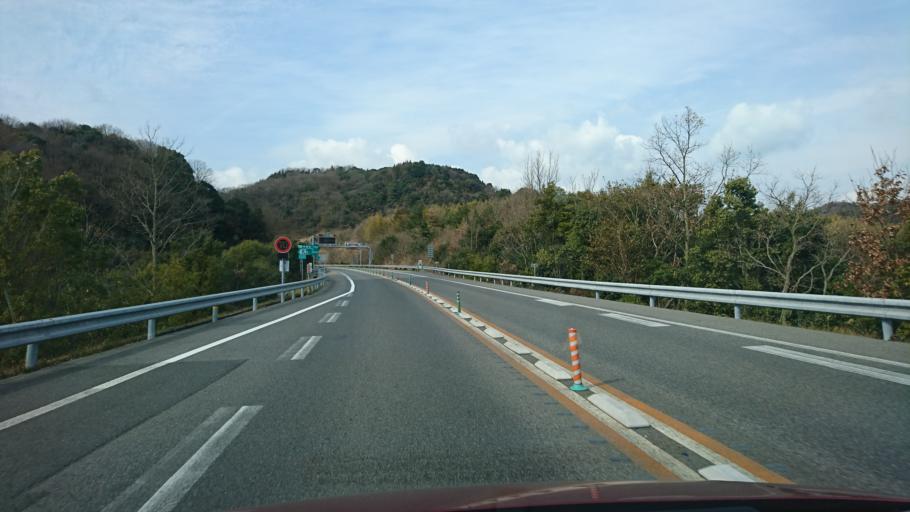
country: JP
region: Hiroshima
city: Innoshima
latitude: 34.1305
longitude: 133.0304
